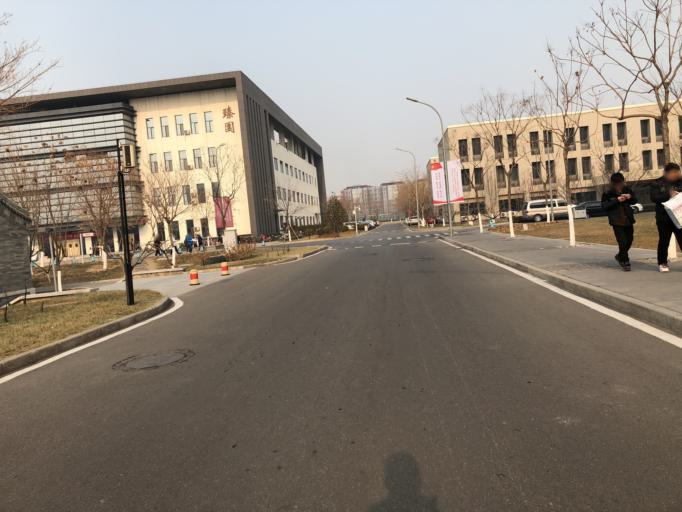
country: CN
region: Beijing
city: Daxing
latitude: 39.7465
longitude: 116.2824
